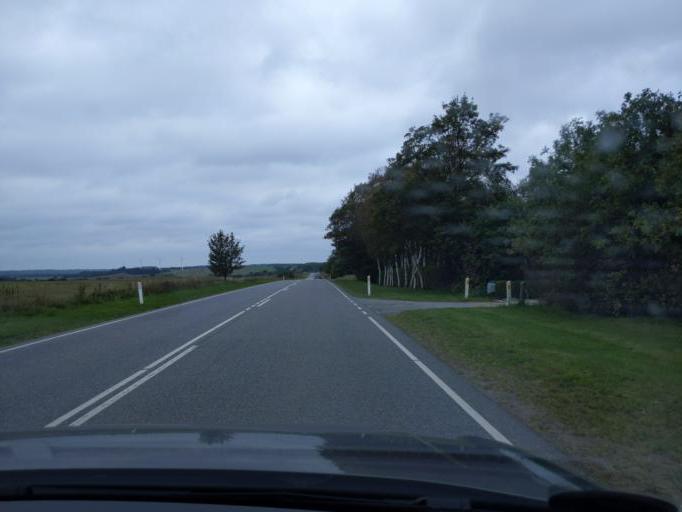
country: DK
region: North Denmark
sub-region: Mariagerfjord Kommune
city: Hobro
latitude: 56.5625
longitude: 9.8407
